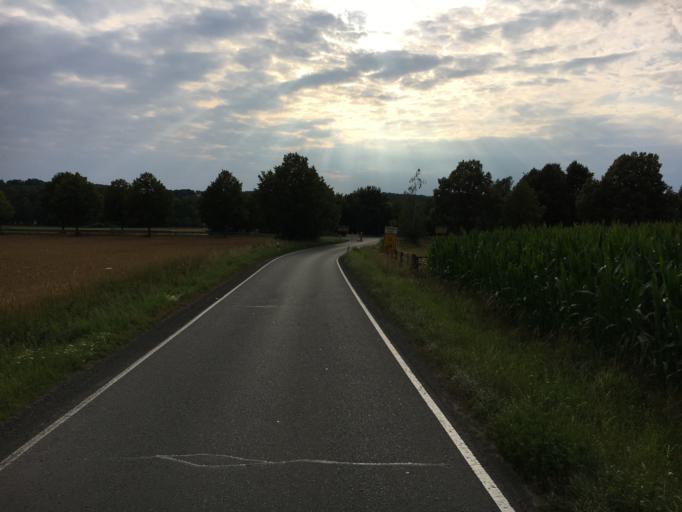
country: DE
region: Hesse
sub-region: Regierungsbezirk Kassel
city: Schrecksbach
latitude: 50.8521
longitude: 9.2940
